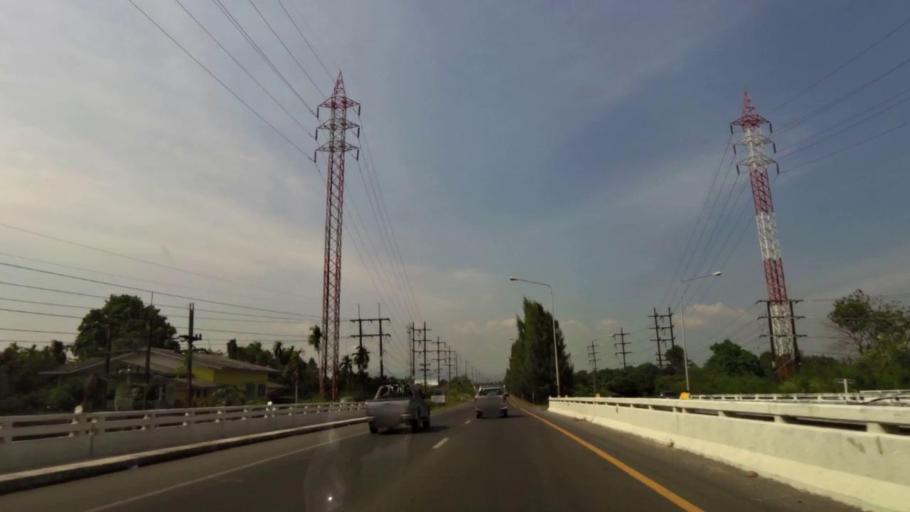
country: TH
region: Chanthaburi
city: Chanthaburi
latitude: 12.6369
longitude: 102.1374
